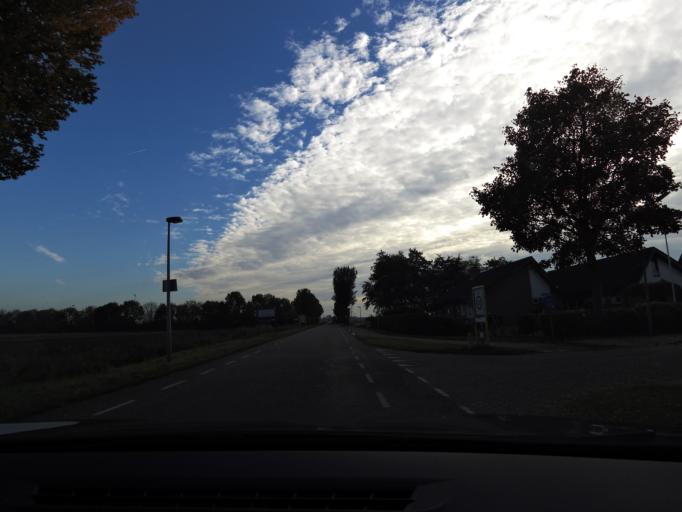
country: NL
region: North Brabant
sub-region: Gemeente Steenbergen
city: Dinteloord
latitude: 51.7132
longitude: 4.2897
